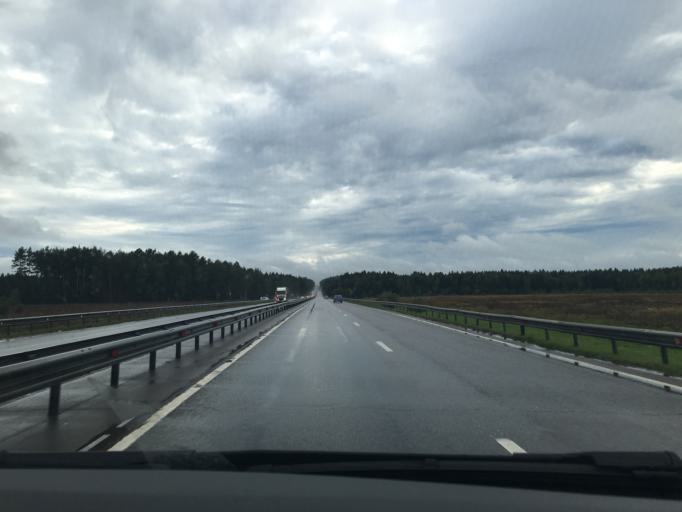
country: RU
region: Kaluga
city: Obninsk
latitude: 55.0339
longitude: 36.5831
